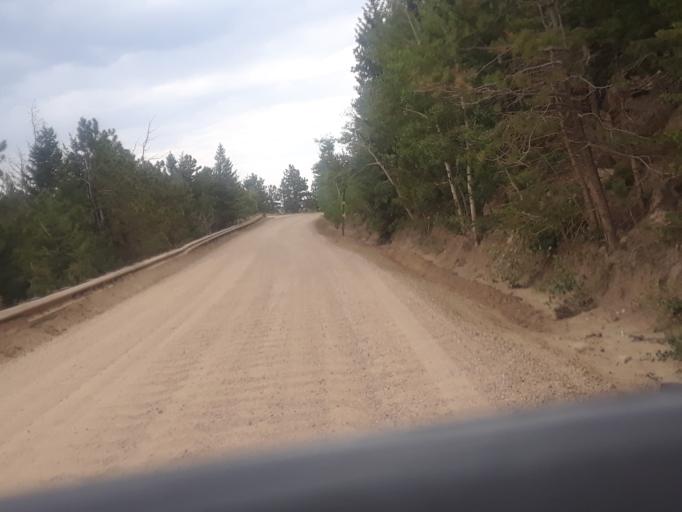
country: US
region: Colorado
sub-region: Boulder County
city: Boulder
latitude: 40.0710
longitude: -105.3888
